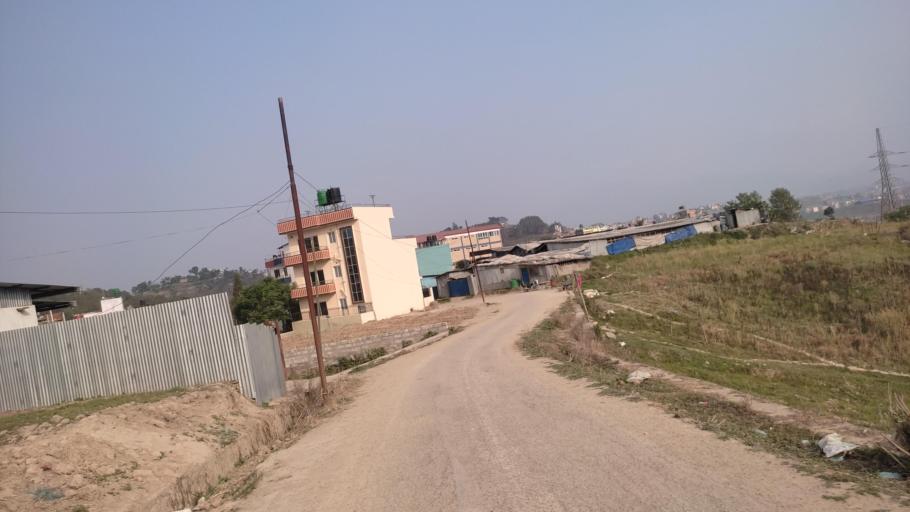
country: NP
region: Central Region
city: Kirtipur
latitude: 27.6598
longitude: 85.2852
